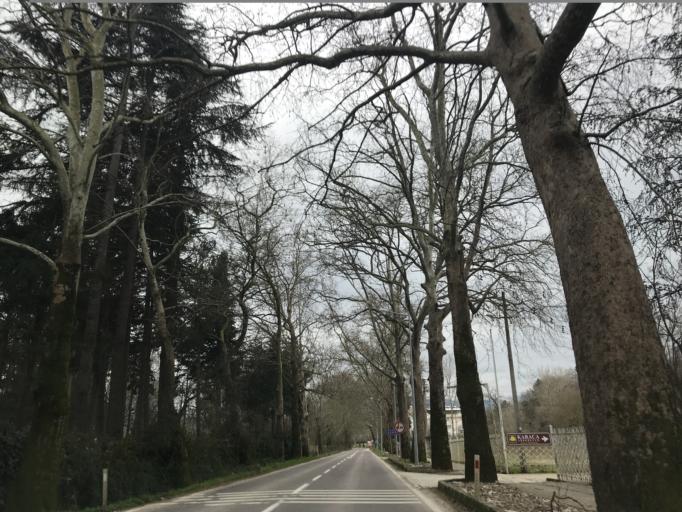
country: TR
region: Yalova
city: Kadikoy
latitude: 40.6340
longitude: 29.2246
